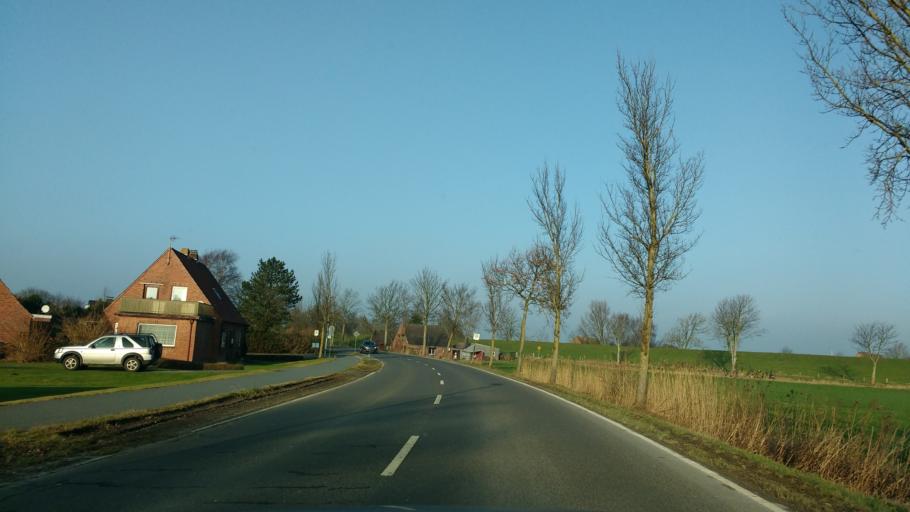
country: DE
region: Schleswig-Holstein
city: Friedrichskoog
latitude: 54.0027
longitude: 8.8874
